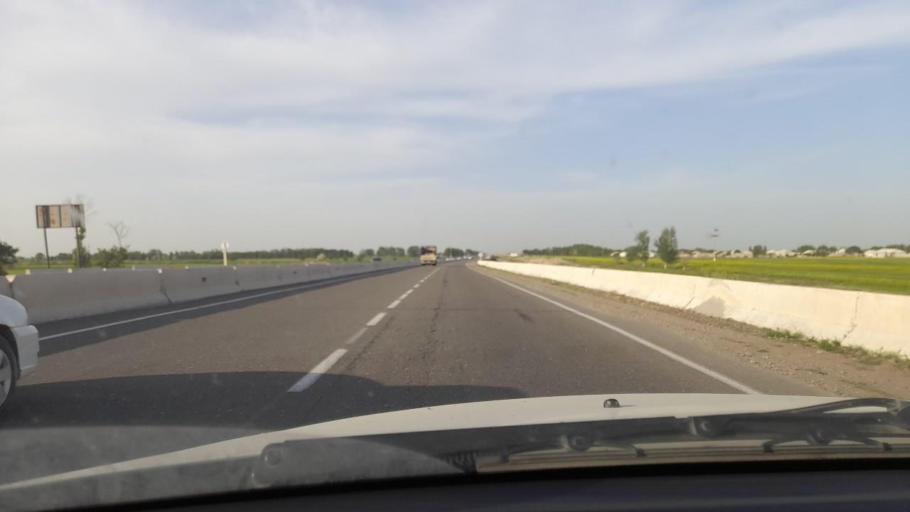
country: UZ
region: Jizzax
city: Paxtakor
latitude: 40.3195
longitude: 68.0945
